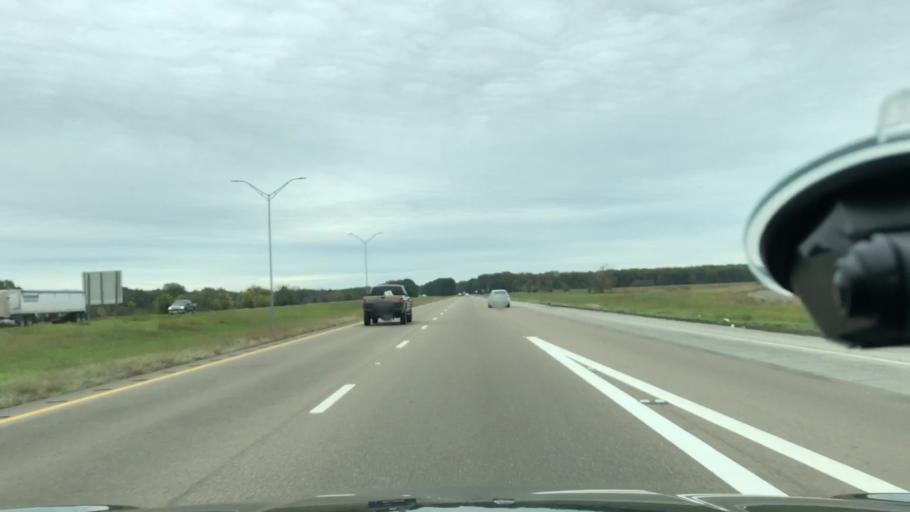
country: US
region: Texas
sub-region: Morris County
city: Naples
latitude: 33.2948
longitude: -94.7322
